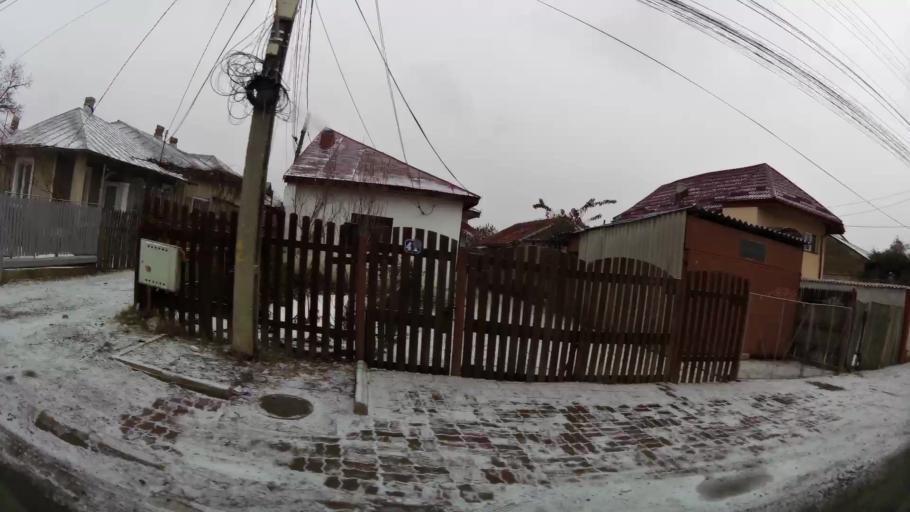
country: RO
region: Dambovita
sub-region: Municipiul Targoviste
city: Targoviste
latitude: 44.9409
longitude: 25.4627
